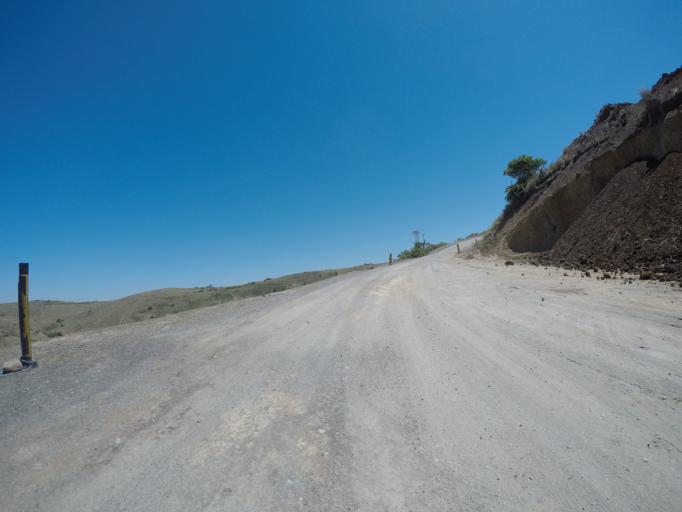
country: ZA
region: Eastern Cape
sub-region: OR Tambo District Municipality
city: Libode
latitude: -32.0123
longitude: 29.0735
